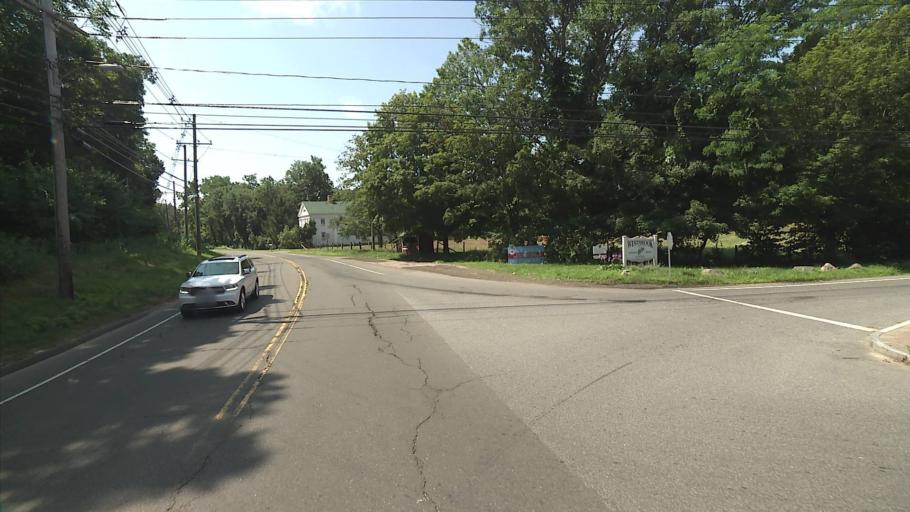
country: US
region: Connecticut
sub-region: Middlesex County
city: Westbrook Center
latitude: 41.3007
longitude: -72.4395
